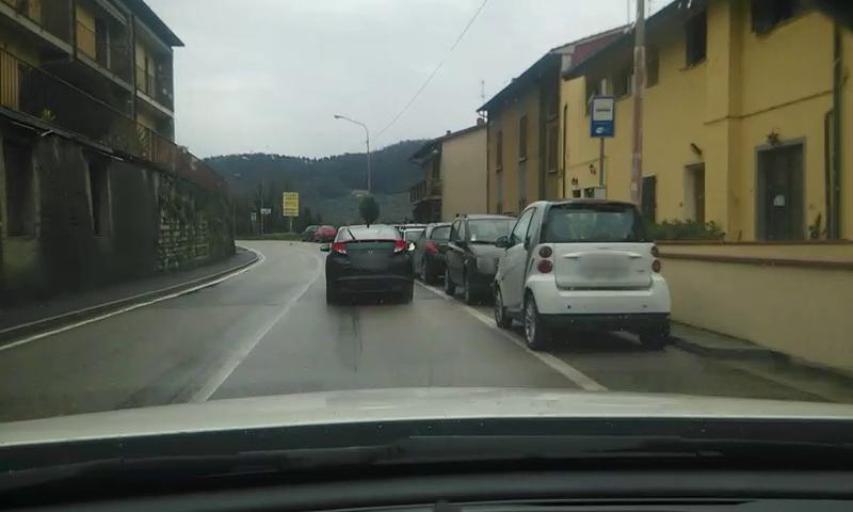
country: IT
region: Tuscany
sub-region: Provincia di Prato
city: Vaiano
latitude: 43.9327
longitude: 11.1266
